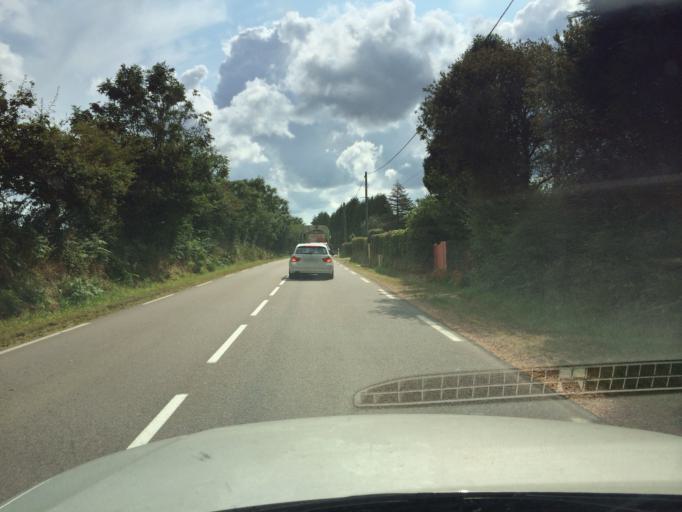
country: FR
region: Lower Normandy
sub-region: Departement de la Manche
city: Tollevast
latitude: 49.5588
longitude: -1.6578
